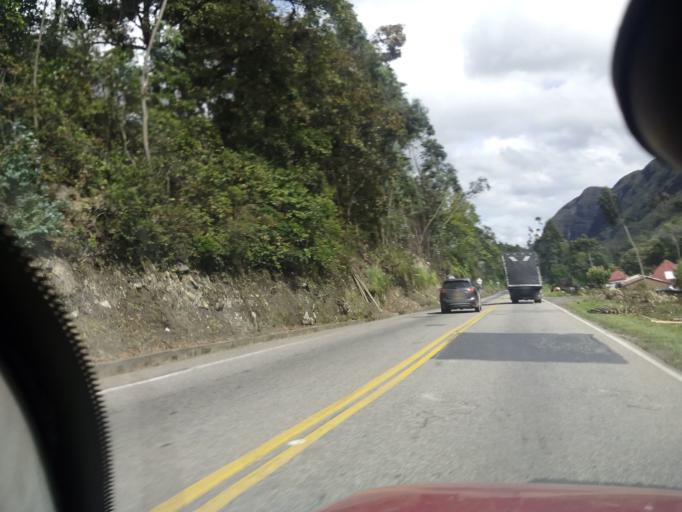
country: CO
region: Boyaca
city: Arcabuco
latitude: 5.7339
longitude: -73.4083
